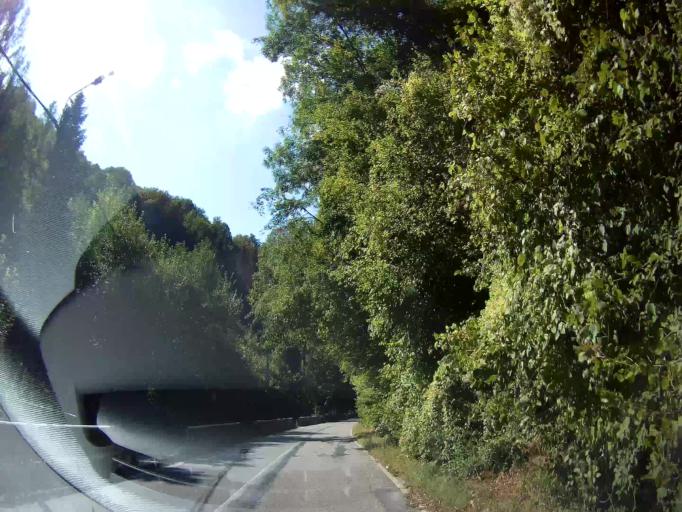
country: BE
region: Wallonia
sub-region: Province de Namur
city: Hastiere-Lavaux
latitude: 50.2224
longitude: 4.8179
